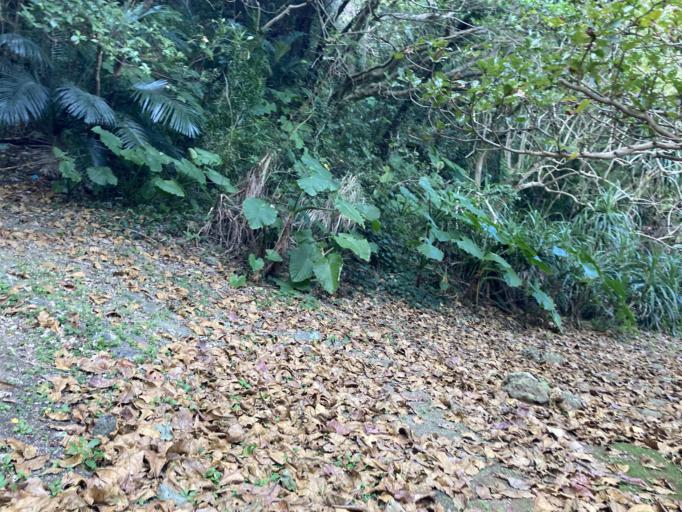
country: JP
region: Okinawa
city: Ishikawa
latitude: 26.4357
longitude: 127.7920
